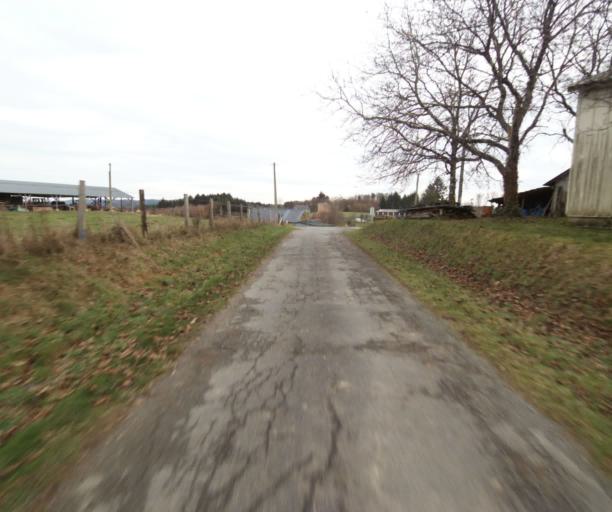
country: FR
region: Limousin
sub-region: Departement de la Correze
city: Cornil
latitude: 45.2275
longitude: 1.6742
